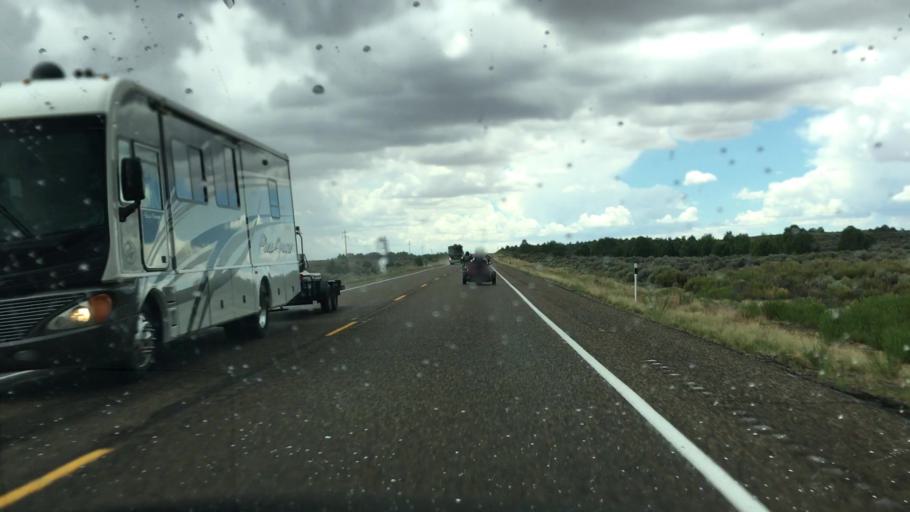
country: US
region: Utah
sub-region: Kane County
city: Kanab
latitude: 37.0773
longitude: -112.1657
